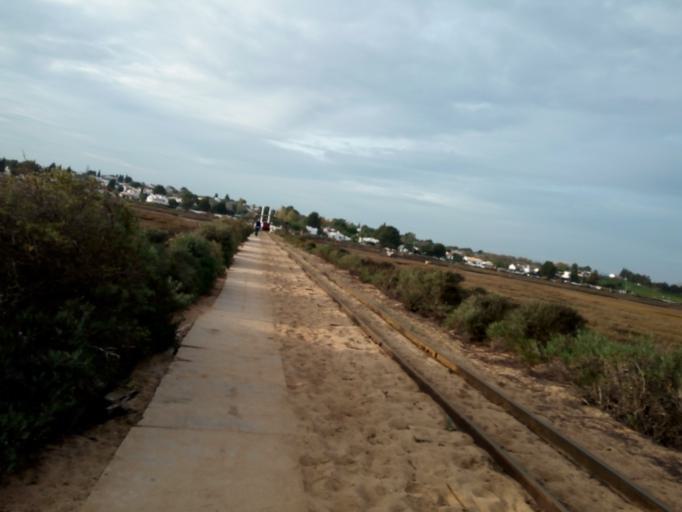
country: PT
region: Faro
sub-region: Tavira
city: Luz
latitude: 37.0907
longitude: -7.6721
